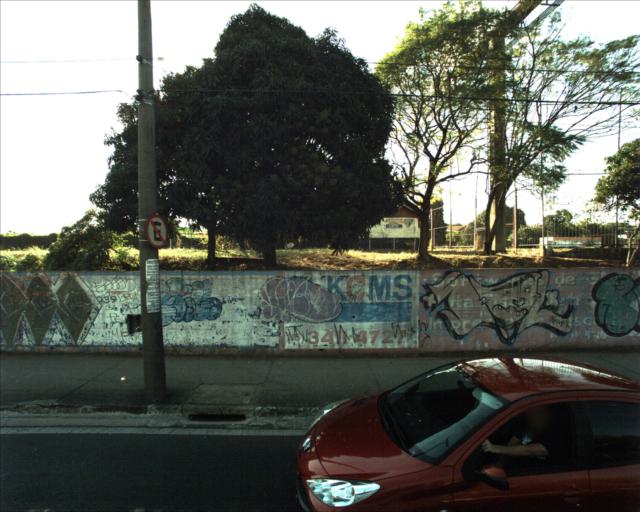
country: BR
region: Sao Paulo
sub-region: Sorocaba
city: Sorocaba
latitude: -23.4944
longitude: -47.4486
